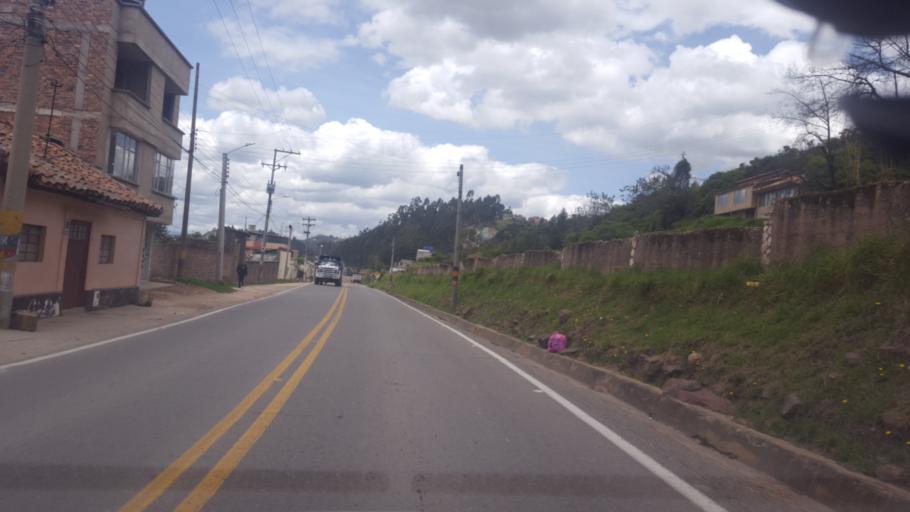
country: CO
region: Boyaca
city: Duitama
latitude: 5.8353
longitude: -73.0212
